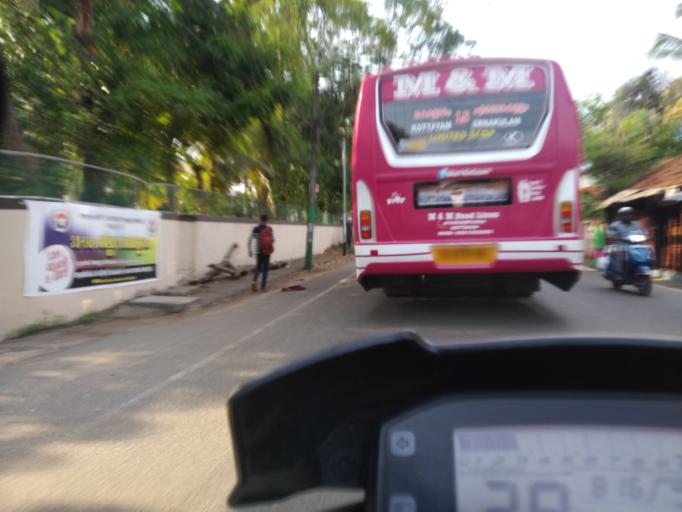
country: IN
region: Kerala
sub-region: Alappuzha
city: Arukutti
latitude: 9.9422
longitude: 76.3501
